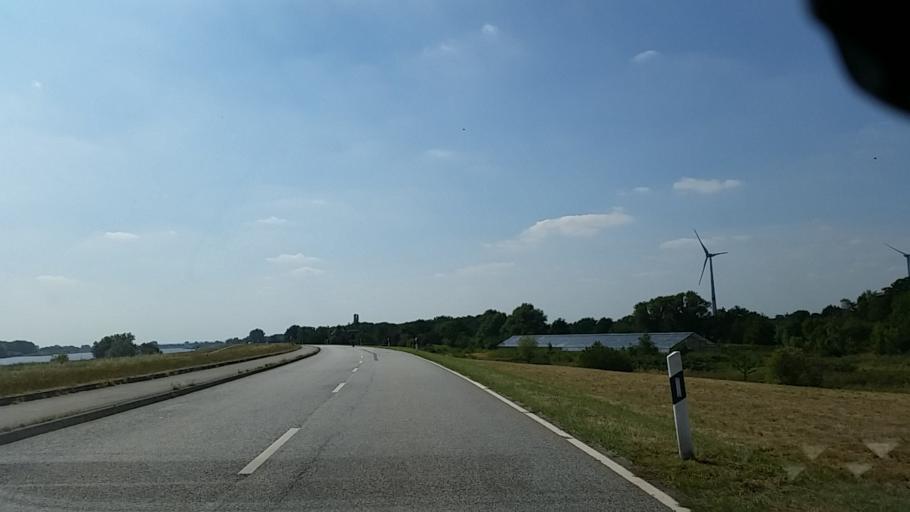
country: DE
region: Lower Saxony
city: Drage
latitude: 53.4222
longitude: 10.2566
